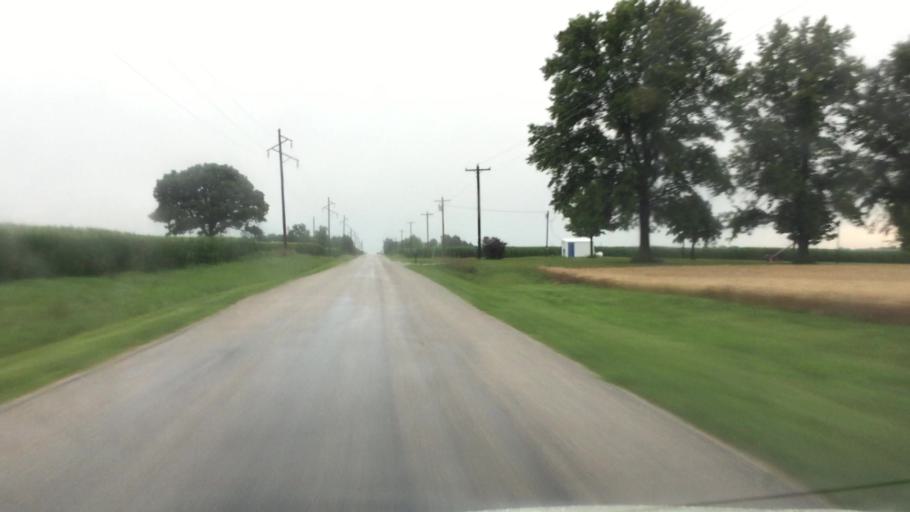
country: US
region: Illinois
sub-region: Hancock County
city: Hamilton
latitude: 40.4337
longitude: -91.2714
